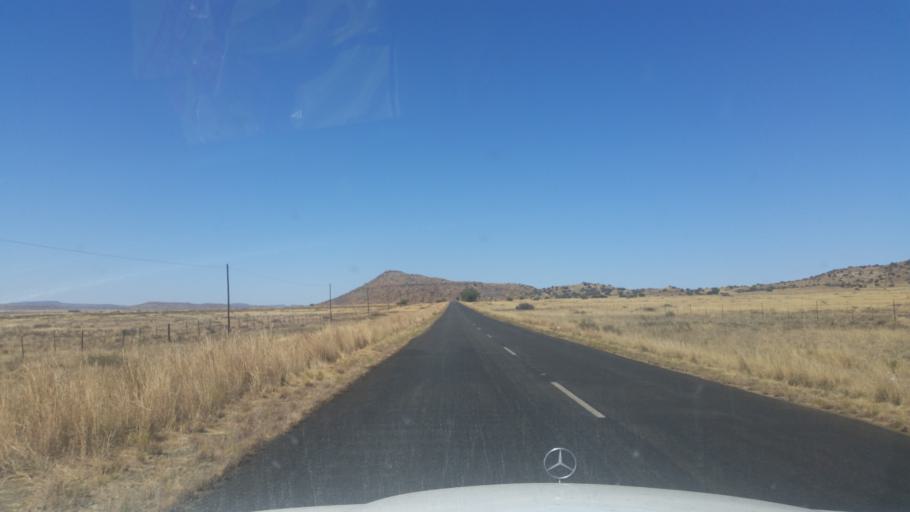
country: ZA
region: Eastern Cape
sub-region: Joe Gqabi District Municipality
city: Burgersdorp
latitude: -30.7282
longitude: 25.7549
